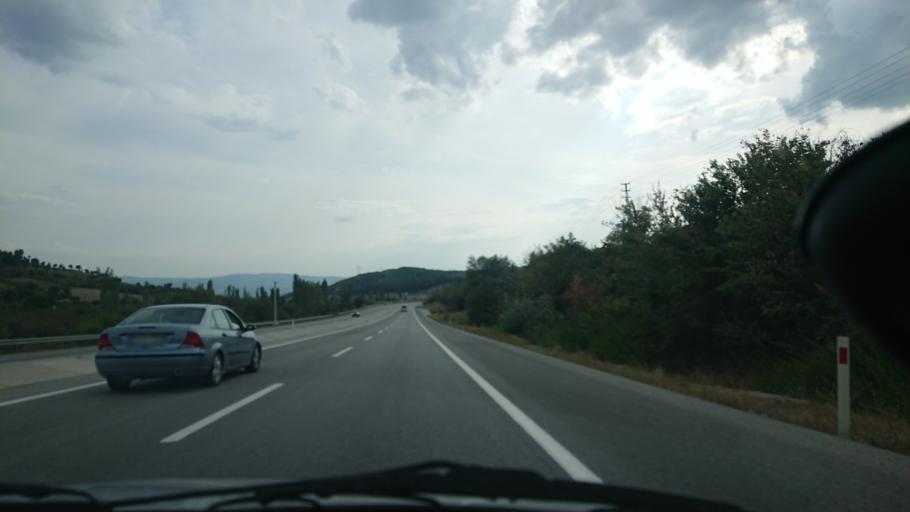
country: TR
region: Kuetahya
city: Gediz
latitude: 39.0388
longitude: 29.4224
